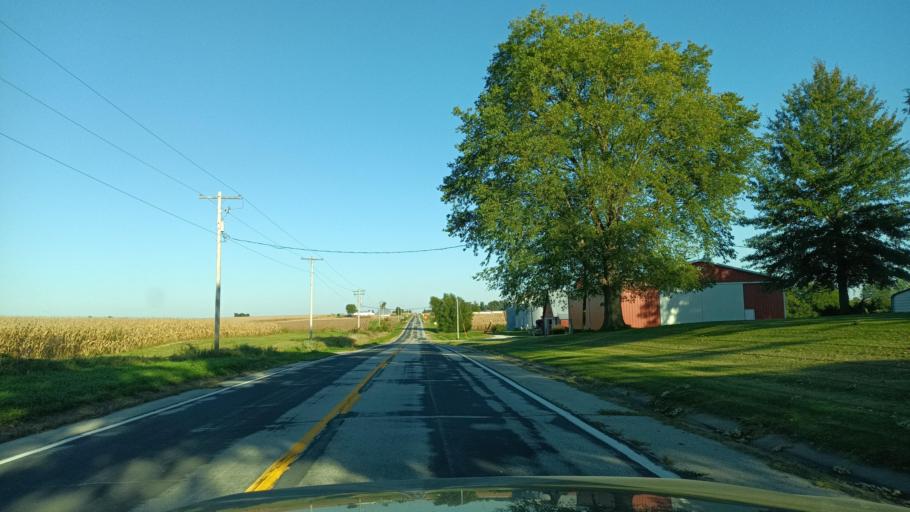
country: US
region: Illinois
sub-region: Warren County
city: Monmouth
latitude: 41.0670
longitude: -90.6401
